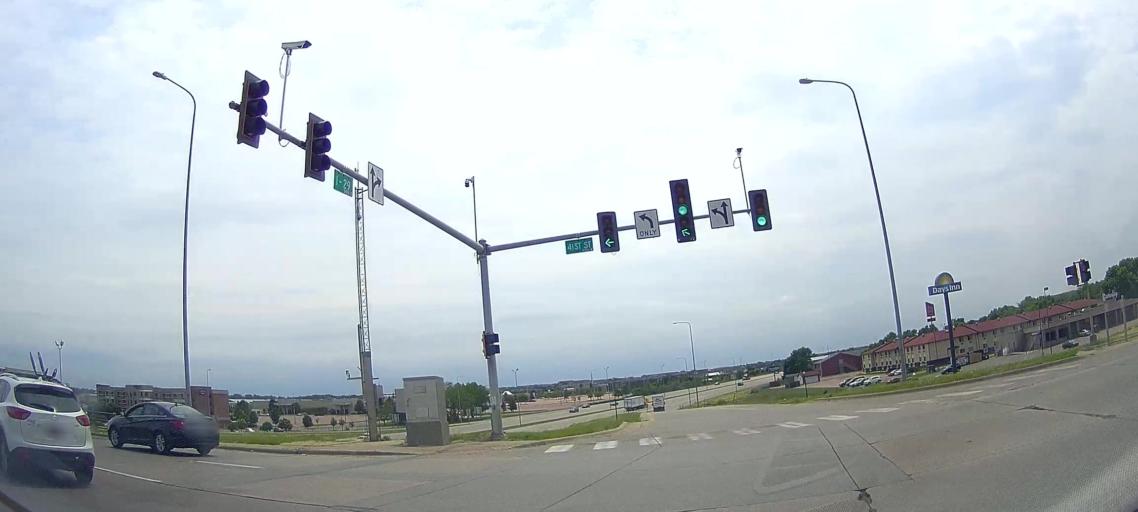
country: US
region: South Dakota
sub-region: Lincoln County
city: Tea
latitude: 43.5150
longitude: -96.7814
